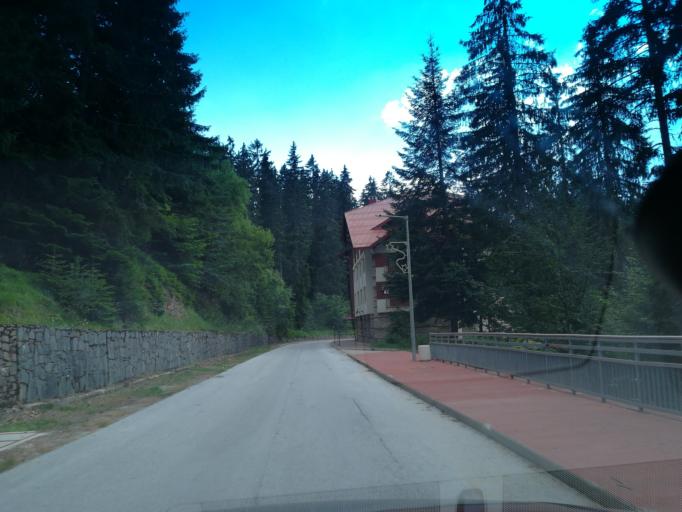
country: BG
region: Smolyan
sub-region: Obshtina Smolyan
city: Smolyan
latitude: 41.6563
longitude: 24.6940
